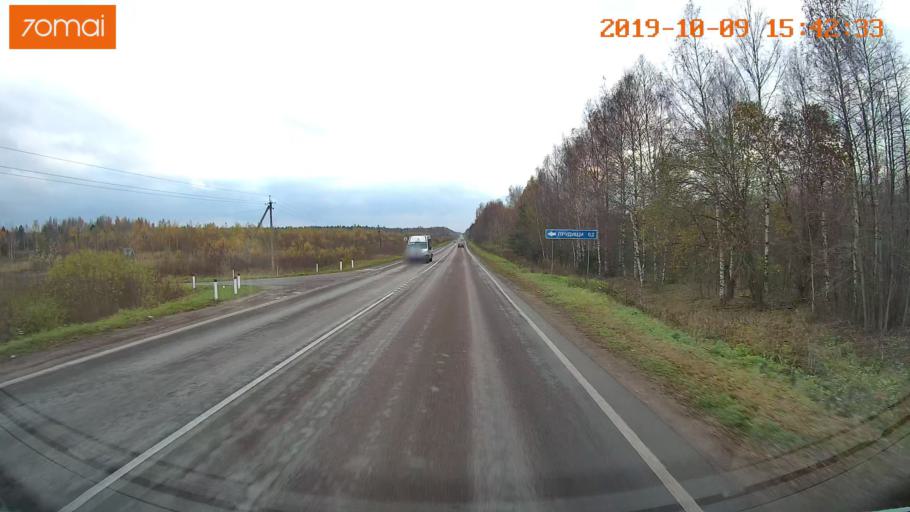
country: RU
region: Kostroma
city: Oktyabr'skiy
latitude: 57.8672
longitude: 41.1049
